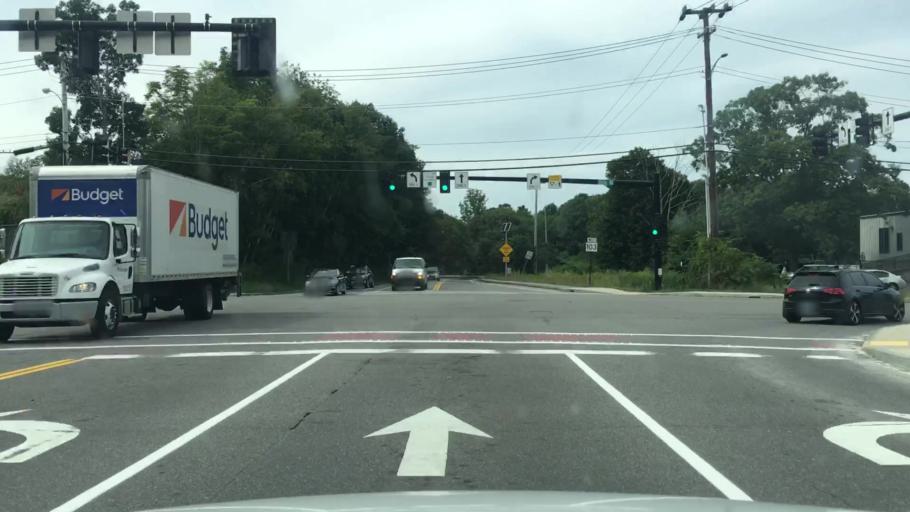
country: US
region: Maine
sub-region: York County
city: Kittery
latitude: 43.0876
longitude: -70.7493
